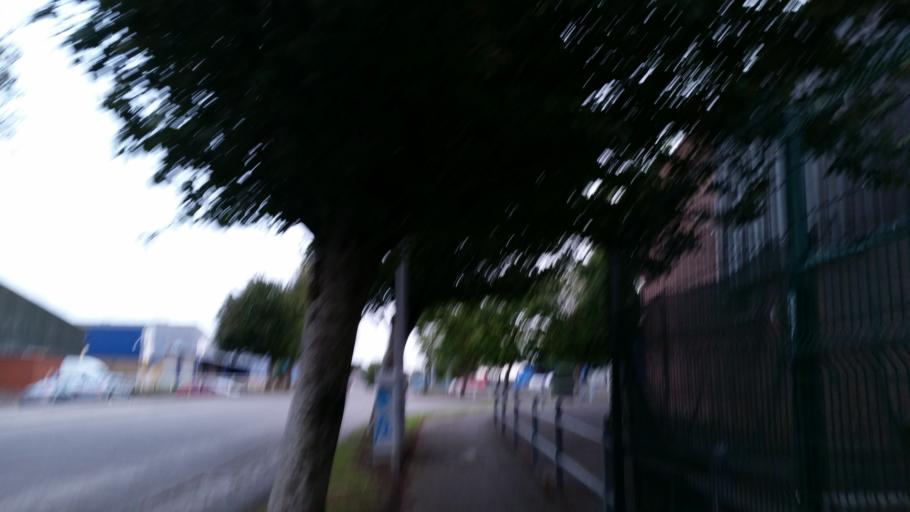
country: IE
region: Leinster
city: Beaumont
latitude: 53.4045
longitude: -6.2378
